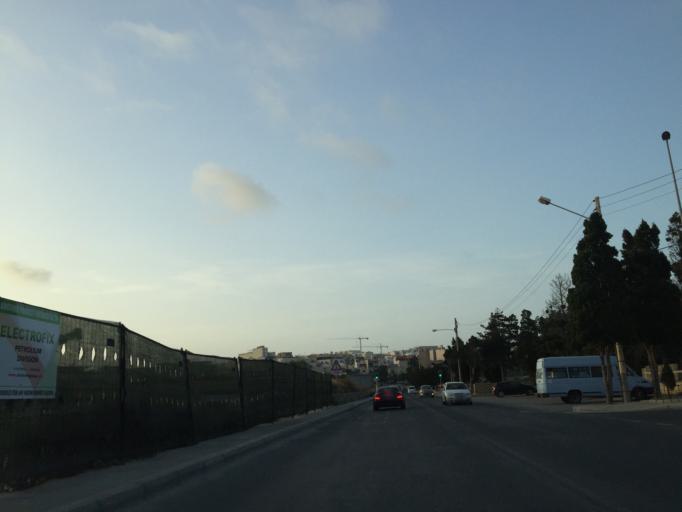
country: MT
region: Saint Paul's Bay
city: San Pawl il-Bahar
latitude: 35.9412
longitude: 14.4115
